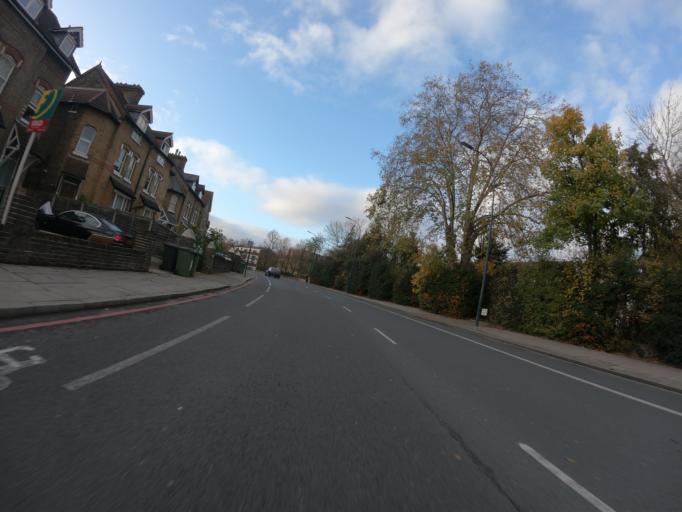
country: GB
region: England
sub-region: Greater London
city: Blackheath
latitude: 51.4580
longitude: 0.0082
